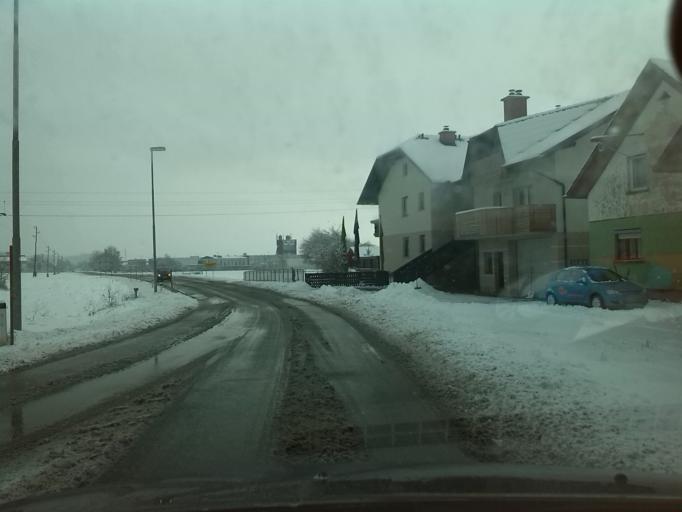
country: SI
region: Kamnik
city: Smarca
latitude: 46.2027
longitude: 14.5762
